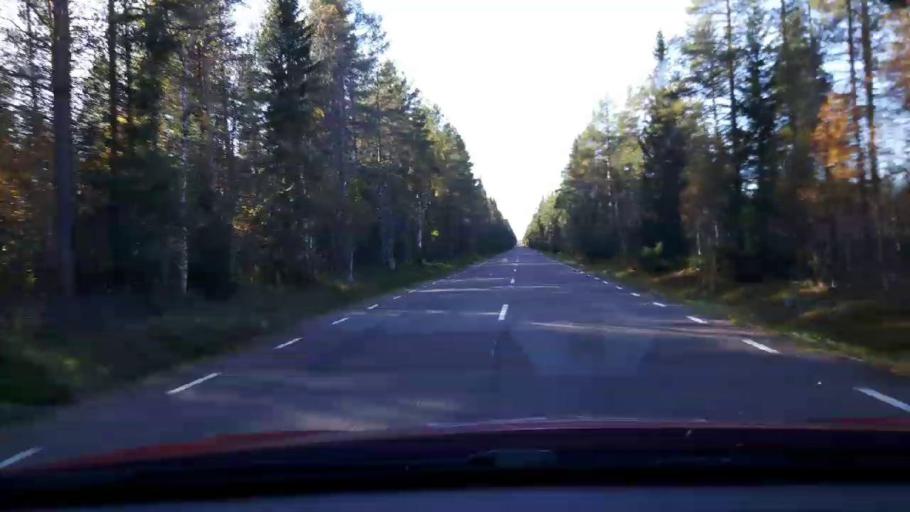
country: SE
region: Jaemtland
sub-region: Stroemsunds Kommun
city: Stroemsund
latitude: 63.8523
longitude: 15.2447
